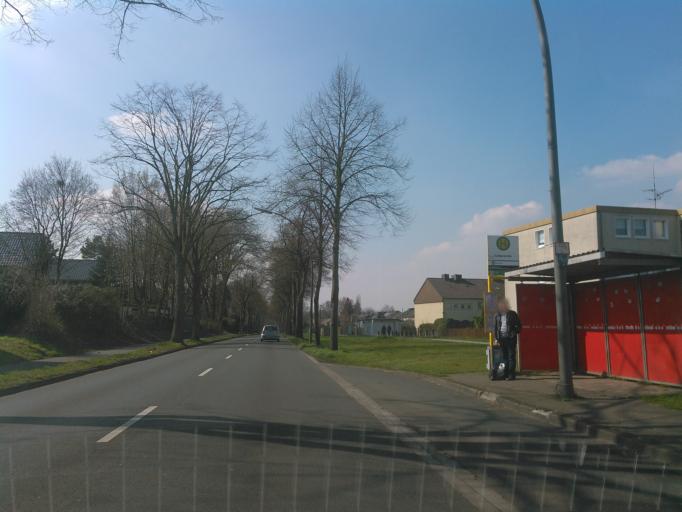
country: DE
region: North Rhine-Westphalia
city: Marl
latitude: 51.6536
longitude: 7.0818
